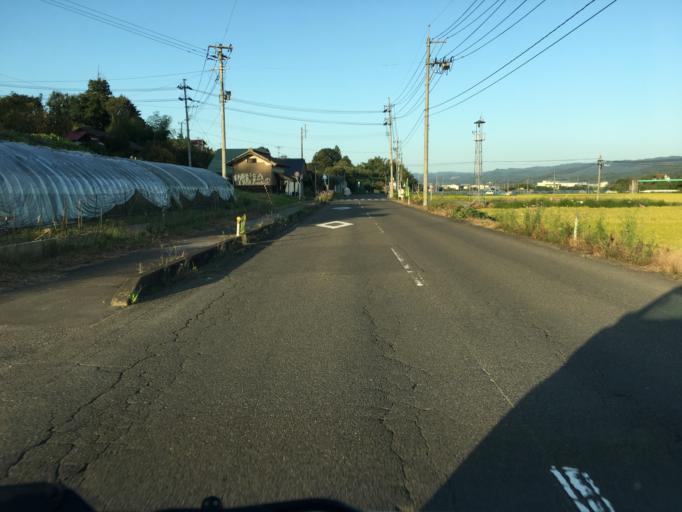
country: JP
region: Fukushima
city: Hobaramachi
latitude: 37.8022
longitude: 140.5459
